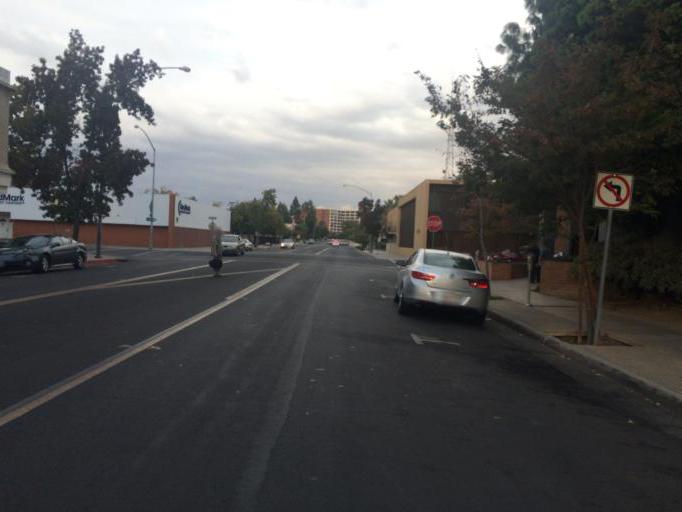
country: US
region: California
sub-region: Fresno County
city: Fresno
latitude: 36.7388
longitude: -119.7908
